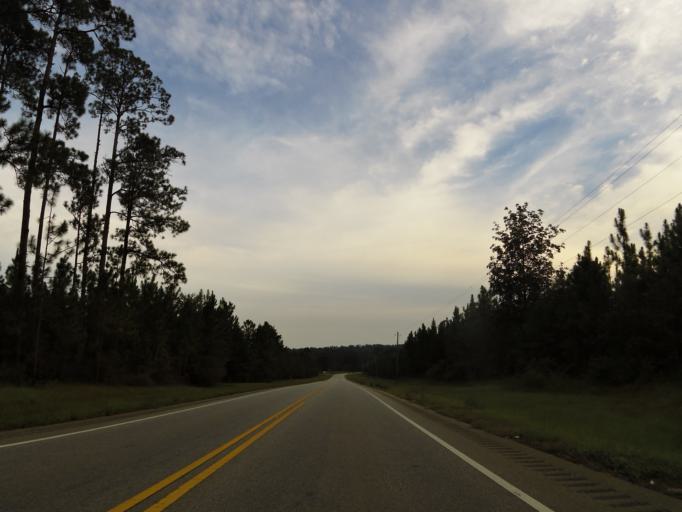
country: US
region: Alabama
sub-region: Monroe County
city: Frisco City
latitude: 31.2637
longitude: -87.4964
